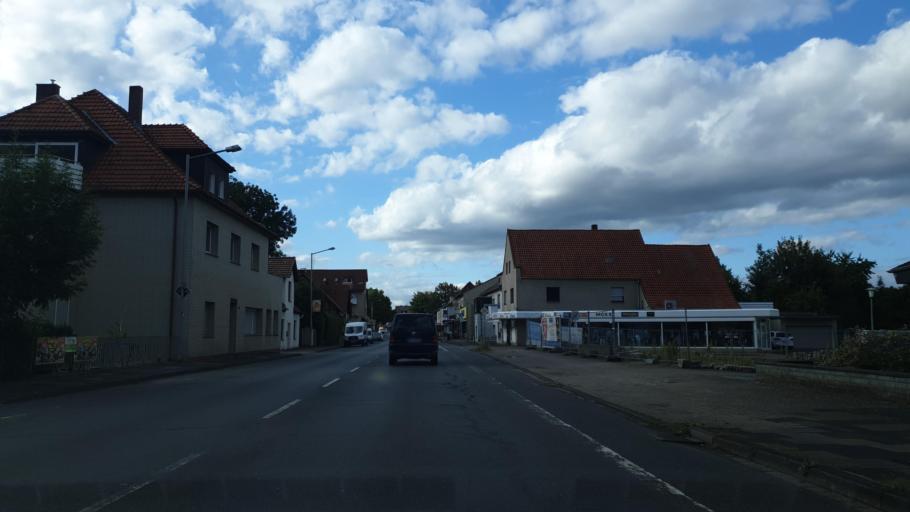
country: DE
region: North Rhine-Westphalia
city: Loehne
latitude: 52.2149
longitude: 8.7127
